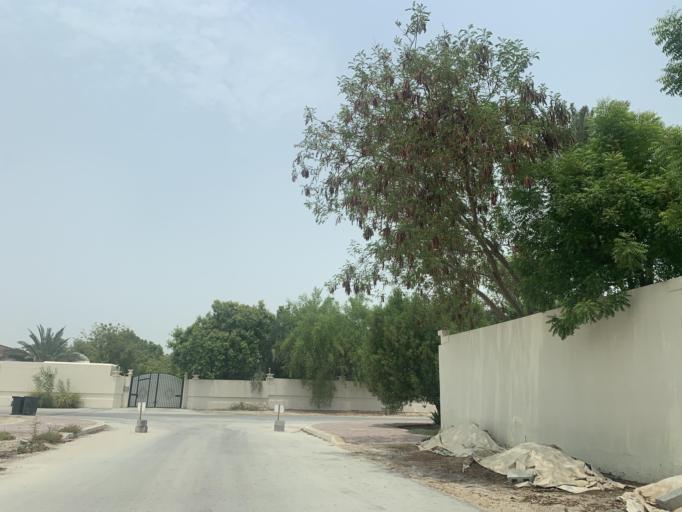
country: BH
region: Central Governorate
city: Madinat Hamad
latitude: 26.1672
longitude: 50.4703
